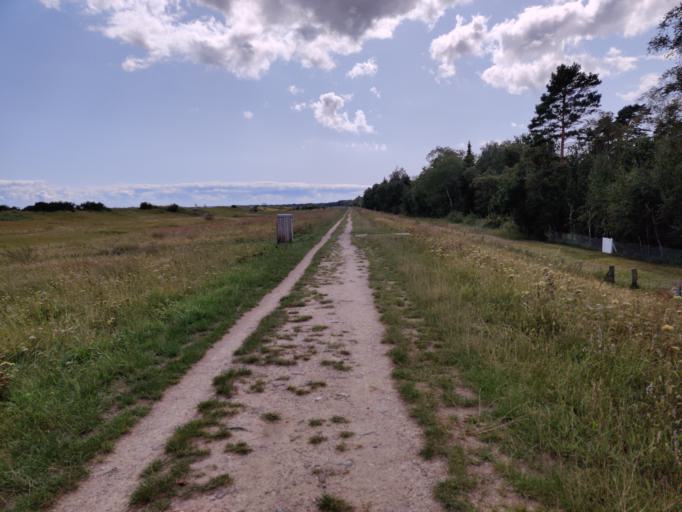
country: DK
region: Zealand
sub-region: Guldborgsund Kommune
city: Nykobing Falster
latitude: 54.6868
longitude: 11.9676
